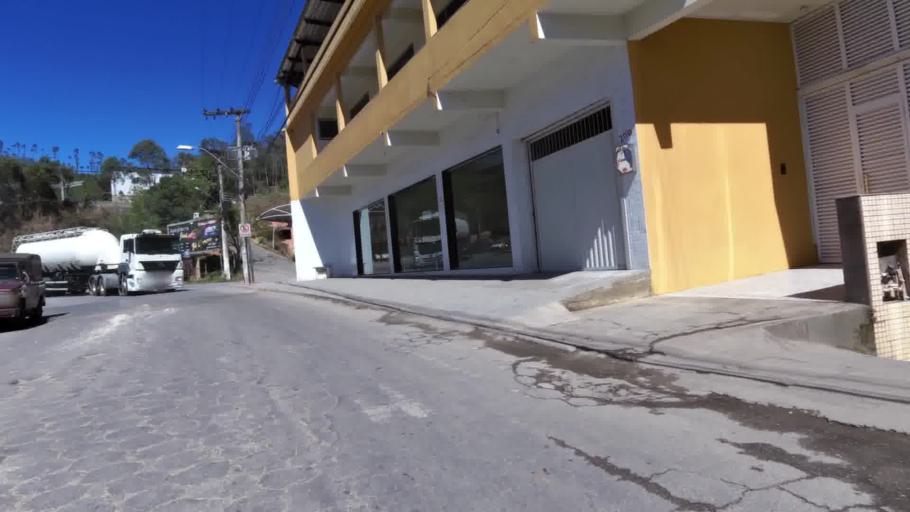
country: BR
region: Espirito Santo
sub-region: Vargem Alta
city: Vargem Alta
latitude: -20.6754
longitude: -41.0127
